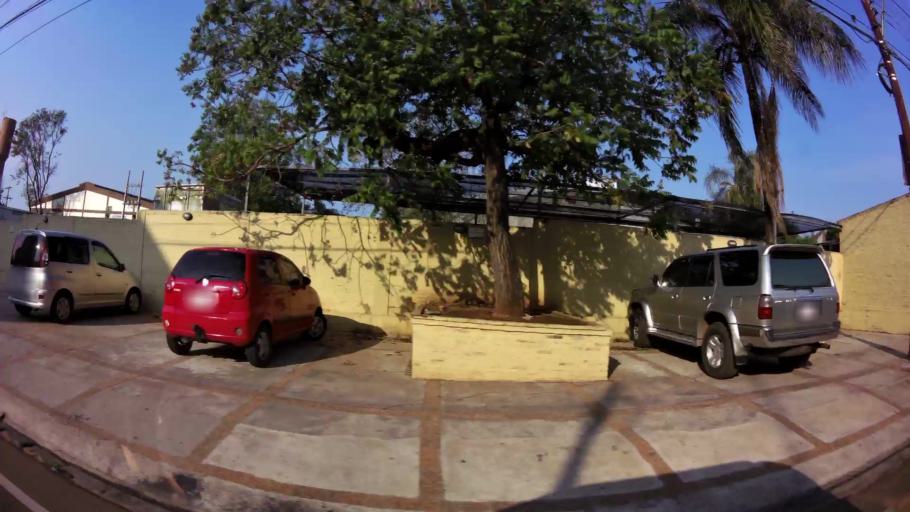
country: PY
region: Central
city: Lambare
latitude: -25.3415
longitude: -57.5906
